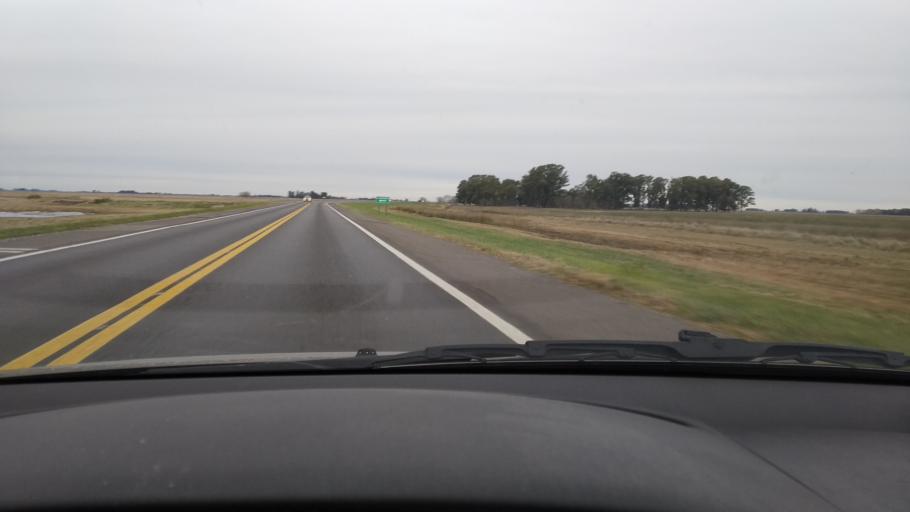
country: AR
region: Buenos Aires
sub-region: Partido de Las Flores
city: Las Flores
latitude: -36.1755
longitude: -59.2458
